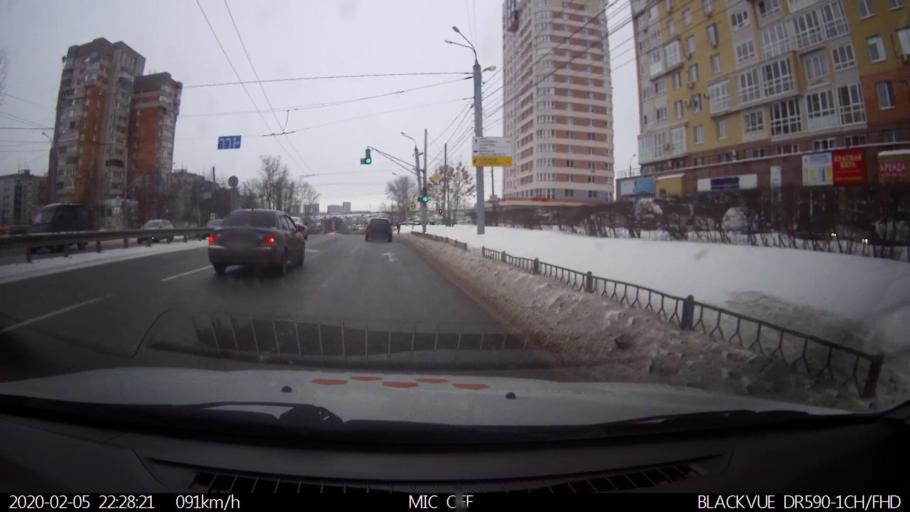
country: RU
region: Nizjnij Novgorod
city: Imeni Stepana Razina
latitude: 54.7581
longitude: 44.1315
